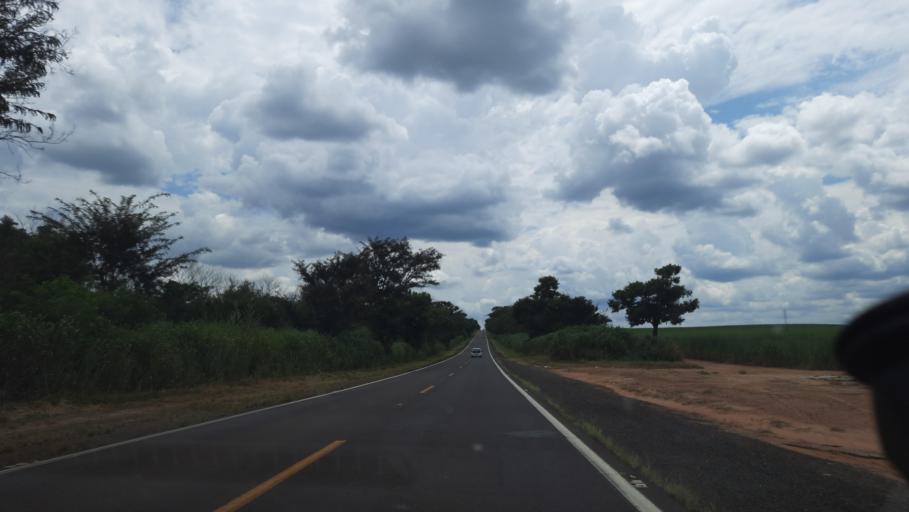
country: BR
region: Sao Paulo
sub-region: Mococa
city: Mococa
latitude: -21.4625
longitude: -47.1066
